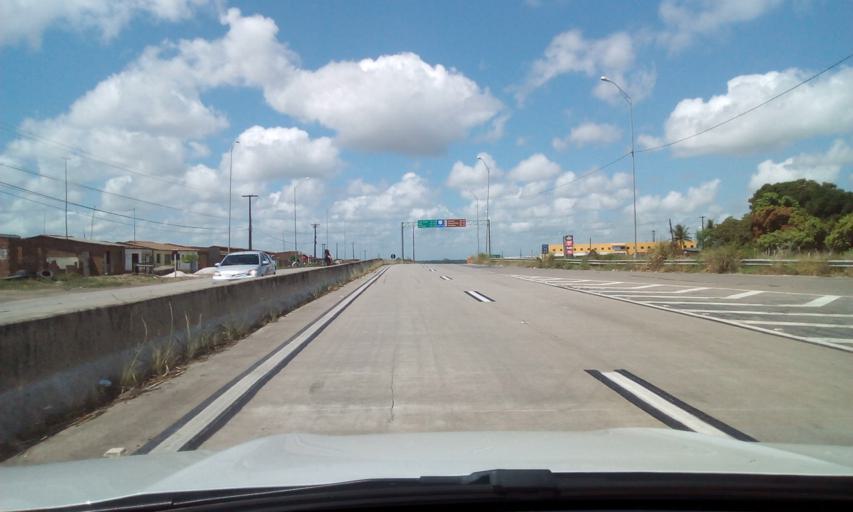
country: BR
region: Pernambuco
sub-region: Goiana
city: Goiana
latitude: -7.4963
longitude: -34.9843
